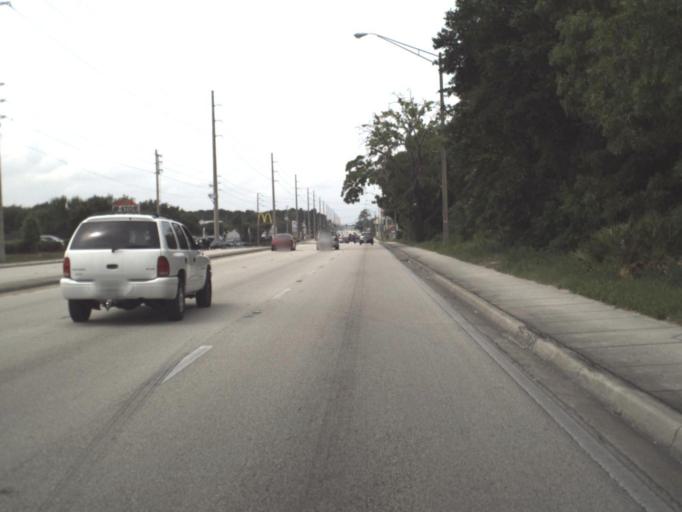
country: US
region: Florida
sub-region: Clay County
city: Lakeside
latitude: 30.1348
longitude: -81.7796
